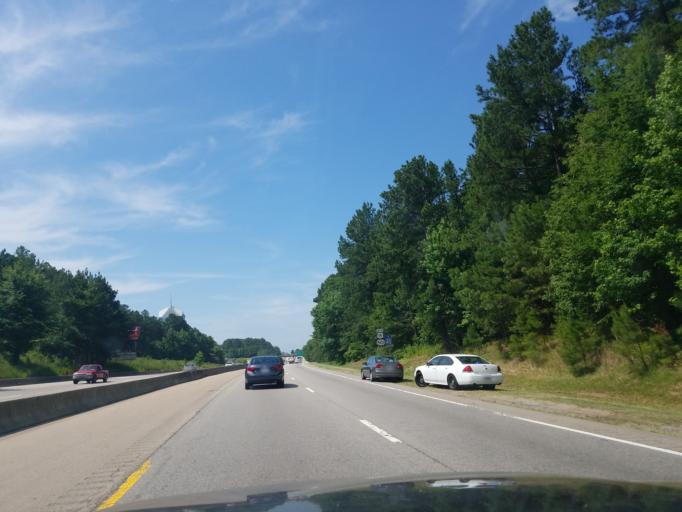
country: US
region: North Carolina
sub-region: Durham County
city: Durham
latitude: 35.9793
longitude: -78.9584
